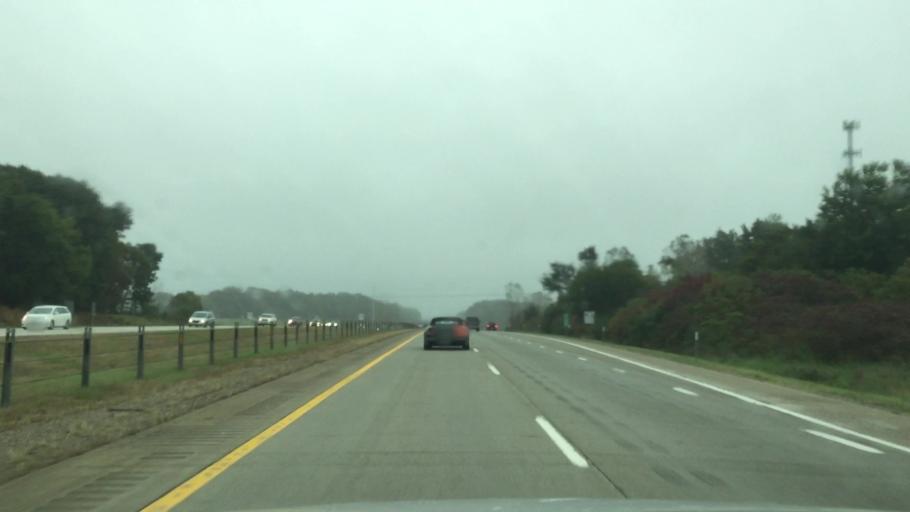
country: US
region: Michigan
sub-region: Van Buren County
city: Paw Paw
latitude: 42.1973
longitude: -85.9726
